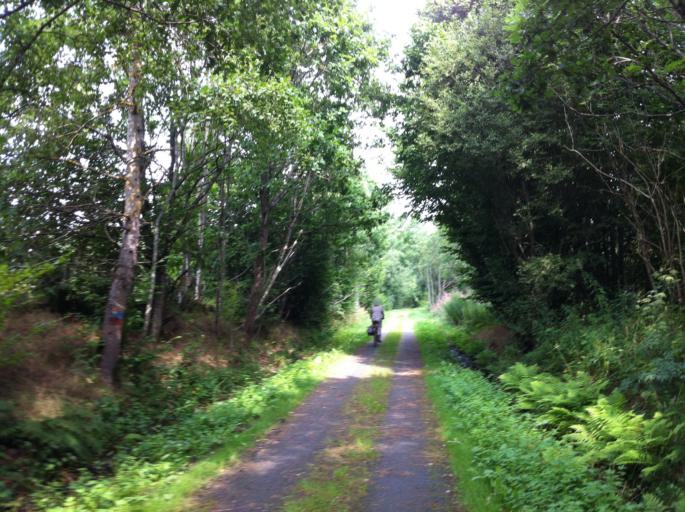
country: SE
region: Skane
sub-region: Hassleholms Kommun
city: Vinslov
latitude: 55.9393
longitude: 13.8274
